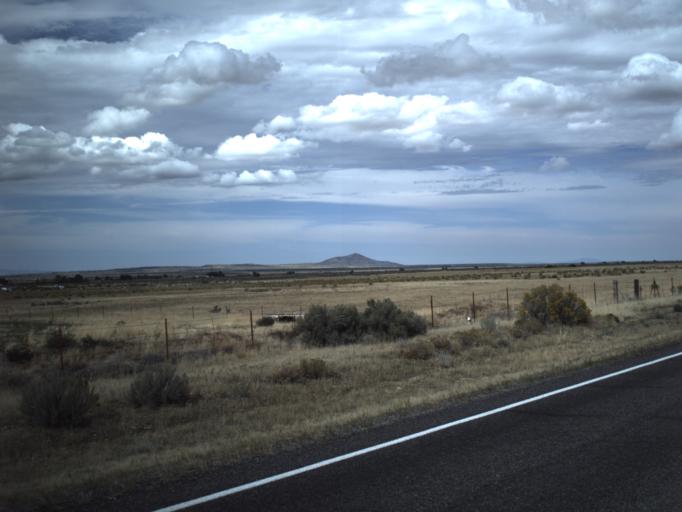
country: US
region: Utah
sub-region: Millard County
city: Fillmore
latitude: 38.9803
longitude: -112.4099
